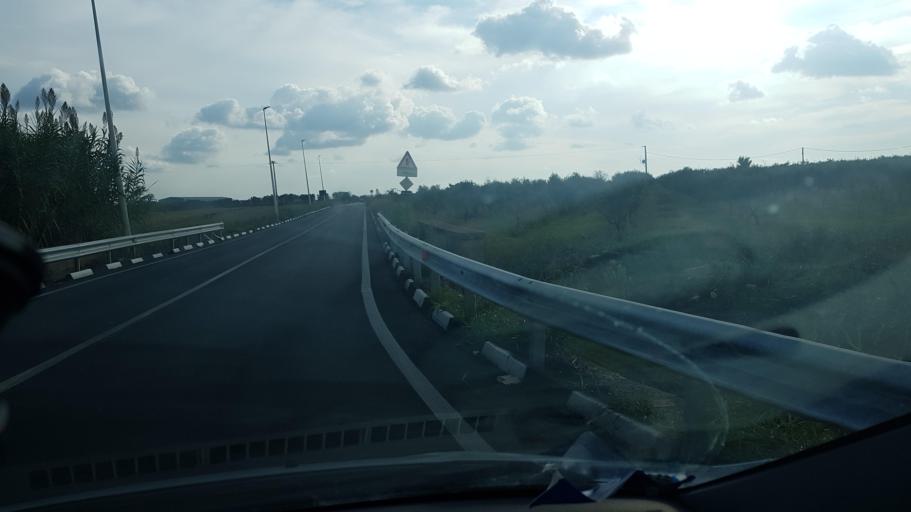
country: IT
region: Apulia
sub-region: Provincia di Brindisi
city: San Donaci
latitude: 40.4387
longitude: 17.9548
